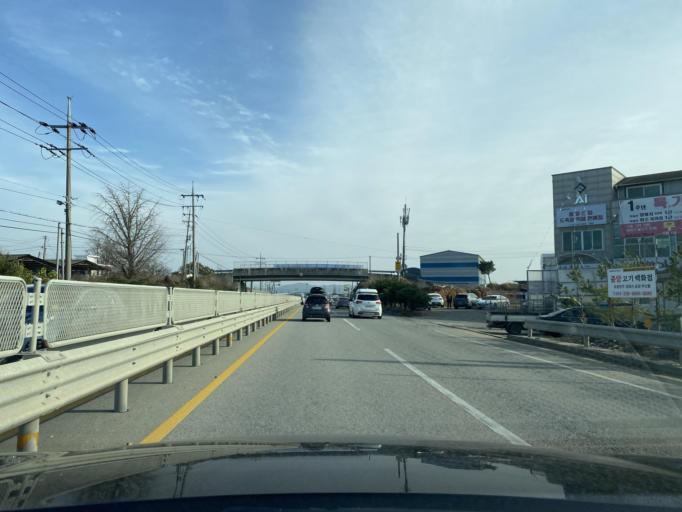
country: KR
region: Chungcheongnam-do
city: Yesan
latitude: 36.6886
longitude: 126.7548
